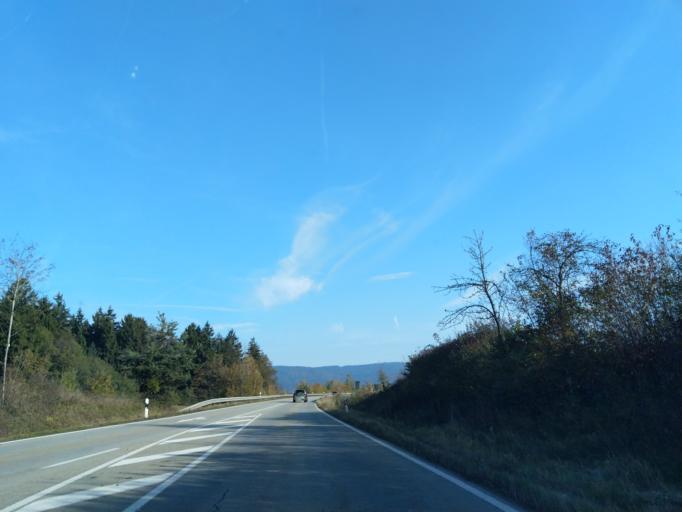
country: DE
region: Bavaria
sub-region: Lower Bavaria
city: Auerbach
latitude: 48.8146
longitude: 13.1200
